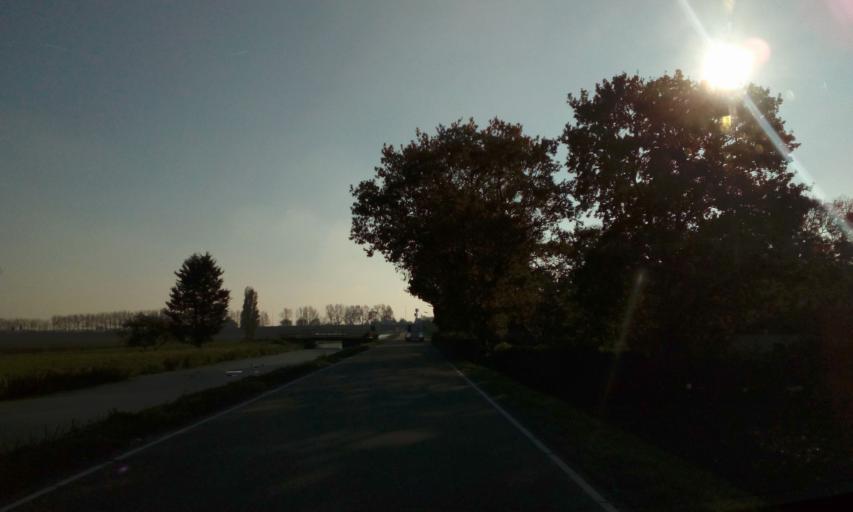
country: NL
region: South Holland
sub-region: Gemeente Lansingerland
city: Bleiswijk
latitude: 52.0318
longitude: 4.5785
